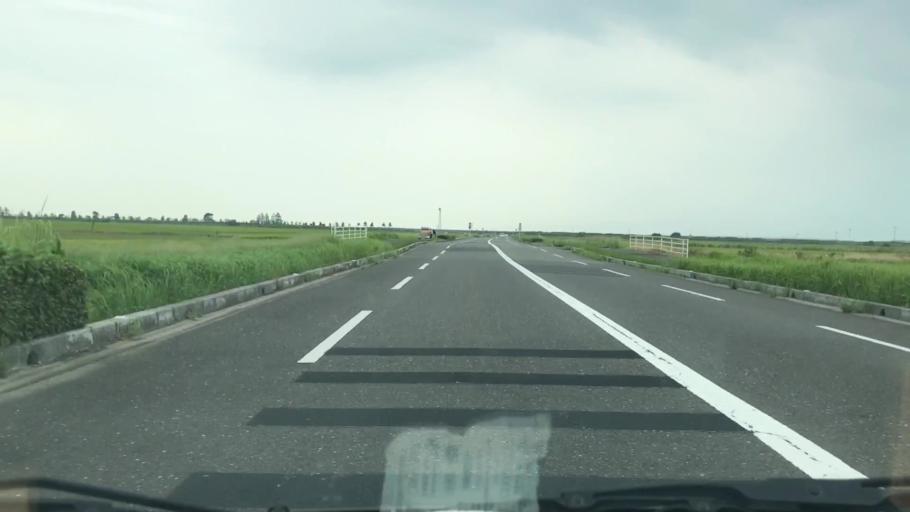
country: JP
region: Saga Prefecture
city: Okawa
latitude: 33.1671
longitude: 130.2930
